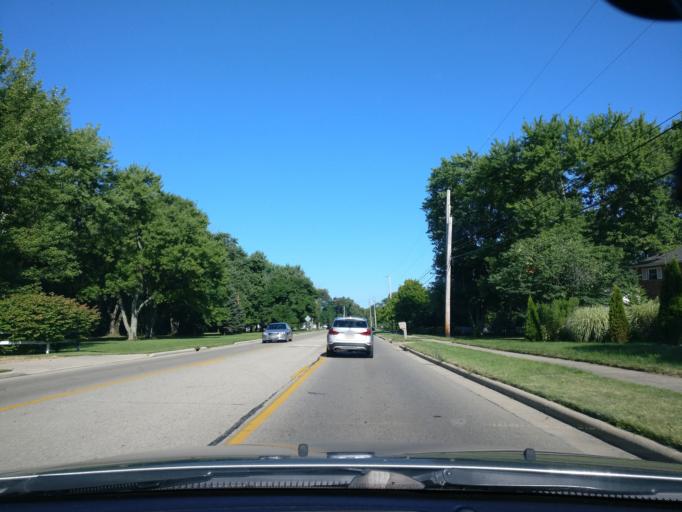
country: US
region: Ohio
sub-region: Montgomery County
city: Centerville
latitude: 39.6140
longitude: -84.1922
